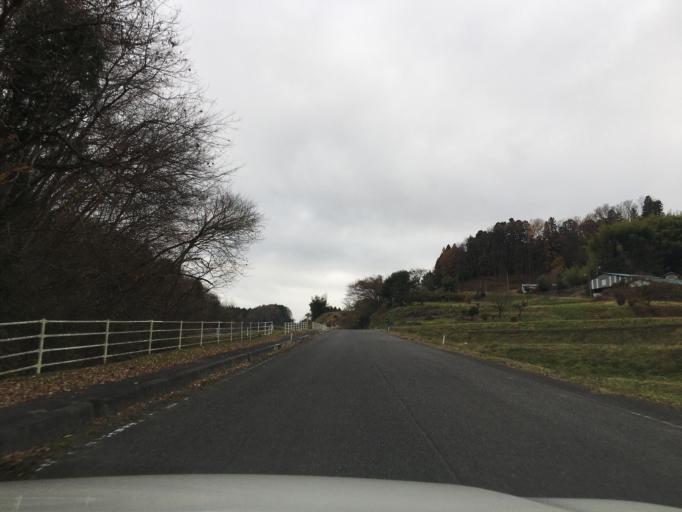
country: JP
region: Fukushima
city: Funehikimachi-funehiki
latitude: 37.4735
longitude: 140.5485
